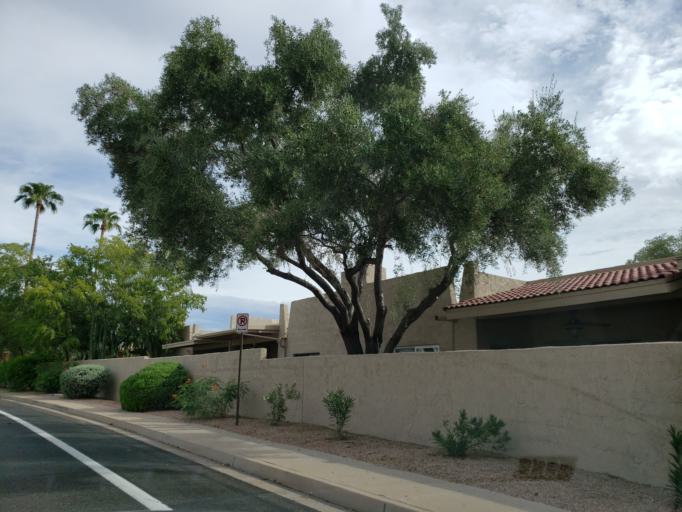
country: US
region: Arizona
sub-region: Maricopa County
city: Scottsdale
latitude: 33.5184
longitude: -111.9131
